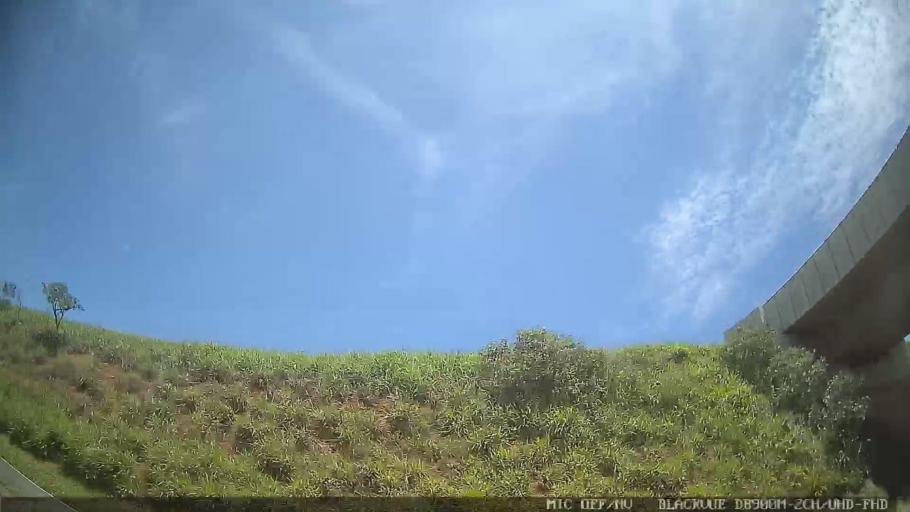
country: BR
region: Sao Paulo
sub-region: Valinhos
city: Valinhos
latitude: -22.9703
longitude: -47.0293
